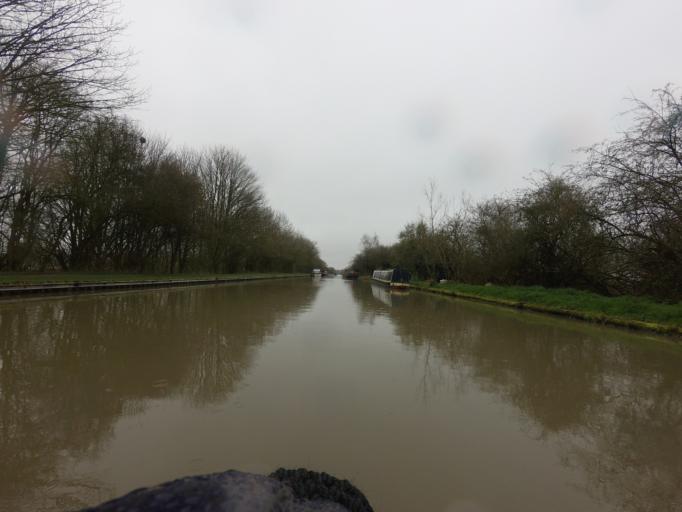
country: GB
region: England
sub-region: Milton Keynes
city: Stony Stratford
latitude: 52.0709
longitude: -0.8378
